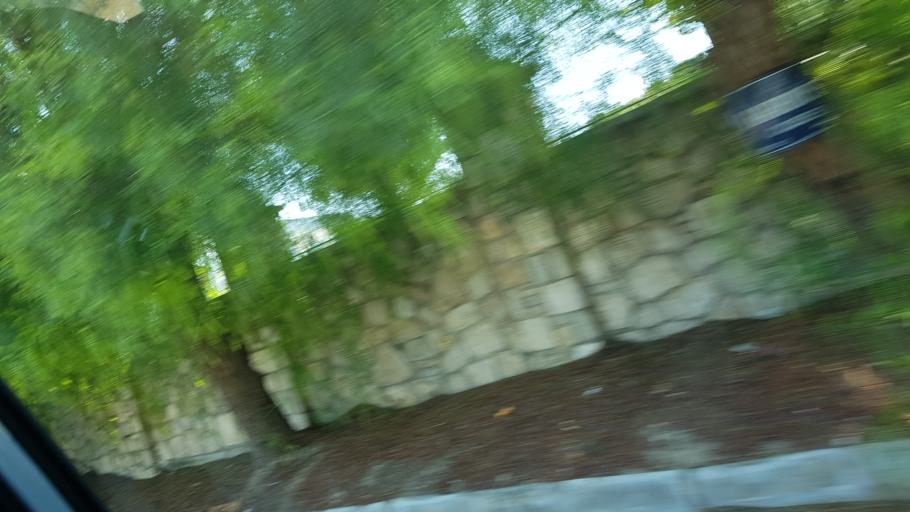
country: TR
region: Izmir
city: Urla
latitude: 38.3808
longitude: 26.7466
